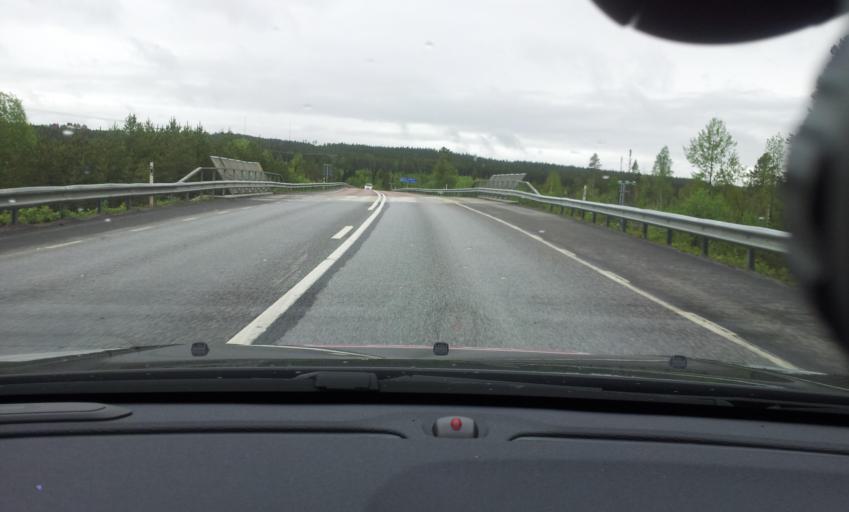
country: SE
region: Jaemtland
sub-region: Krokoms Kommun
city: Valla
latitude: 63.3338
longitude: 13.9763
